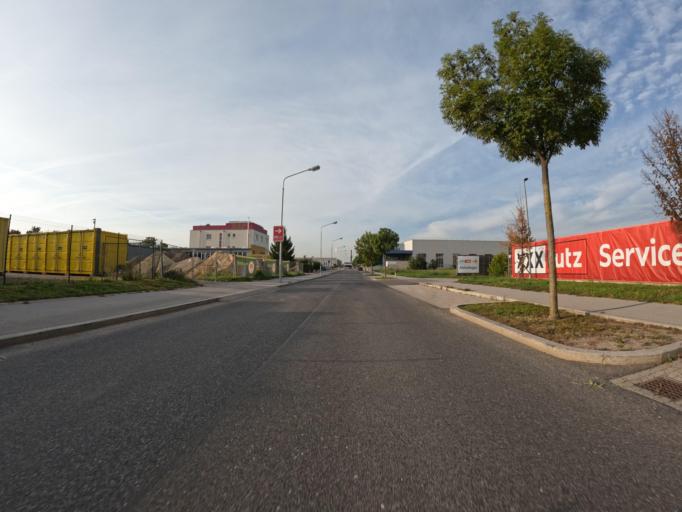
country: AT
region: Lower Austria
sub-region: Politischer Bezirk Wien-Umgebung
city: Gerasdorf bei Wien
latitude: 48.2579
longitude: 16.4690
